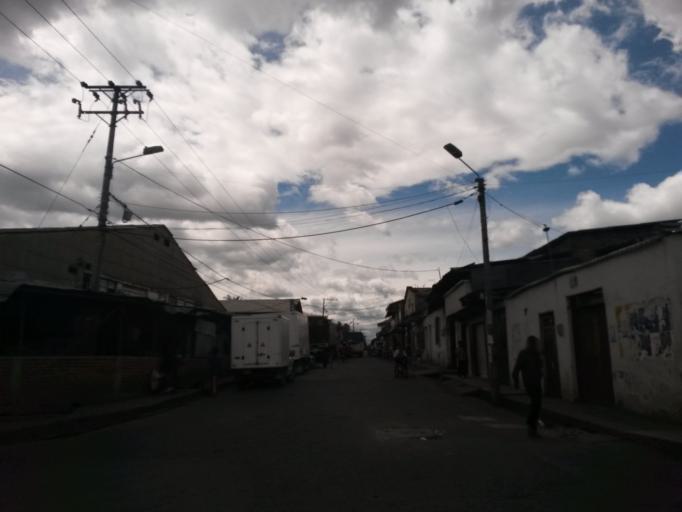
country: CO
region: Cauca
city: Popayan
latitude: 2.4345
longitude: -76.6086
